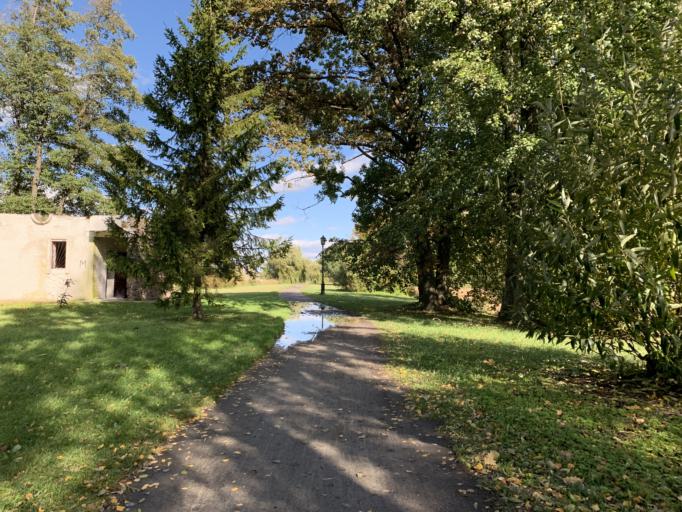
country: BY
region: Minsk
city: Nyasvizh
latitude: 53.2236
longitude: 26.6987
